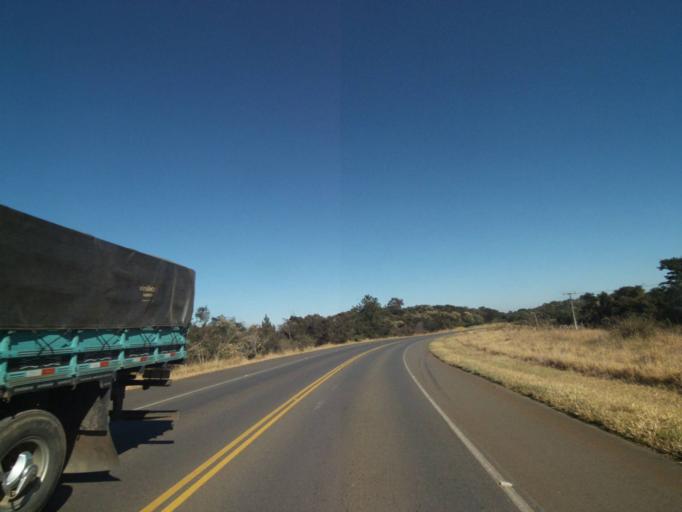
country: BR
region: Parana
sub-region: Tibagi
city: Tibagi
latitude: -24.4108
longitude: -50.3553
